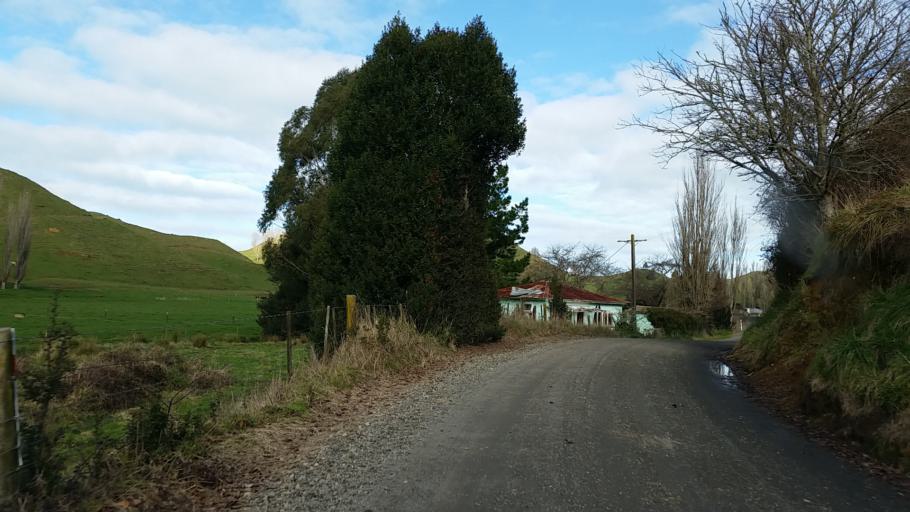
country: NZ
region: Taranaki
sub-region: South Taranaki District
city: Eltham
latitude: -39.2525
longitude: 174.5330
